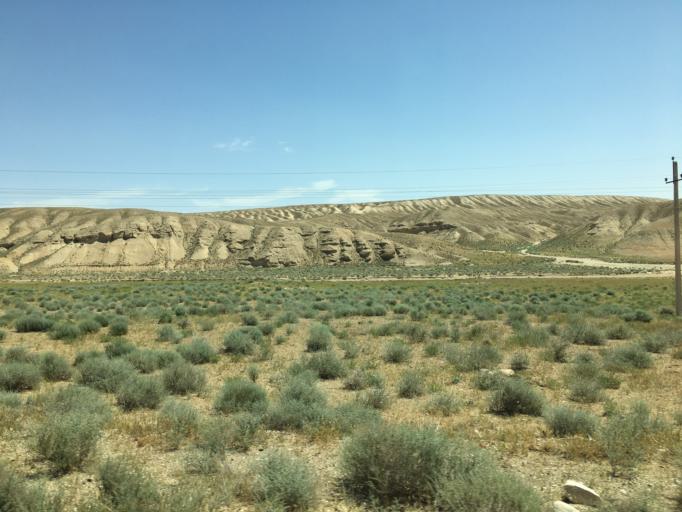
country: TM
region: Balkan
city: Turkmenbasy
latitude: 40.0985
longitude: 53.3662
